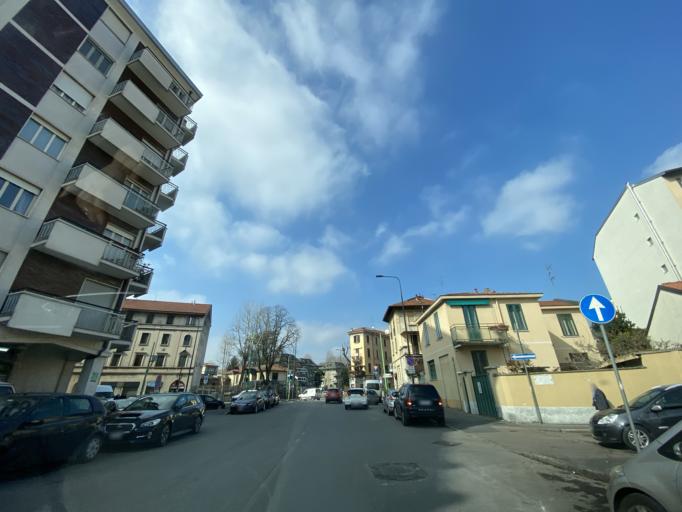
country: IT
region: Lombardy
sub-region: Citta metropolitana di Milano
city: Bresso
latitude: 45.5175
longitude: 9.1923
